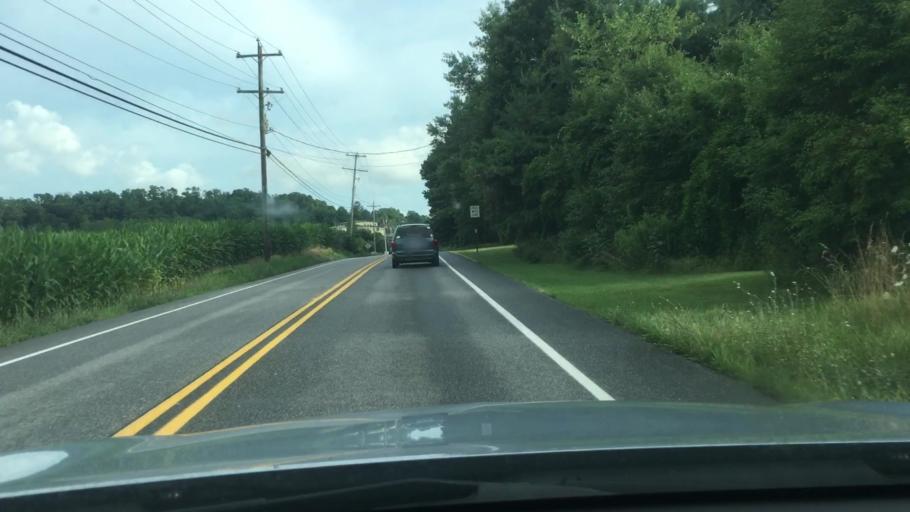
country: US
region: Pennsylvania
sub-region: York County
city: Dillsburg
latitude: 40.1257
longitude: -77.0364
